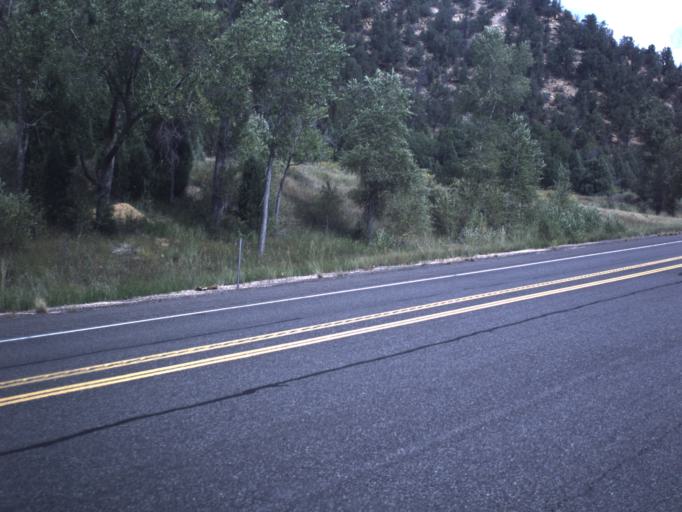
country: US
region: Utah
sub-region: Kane County
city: Kanab
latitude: 37.3806
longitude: -112.5797
